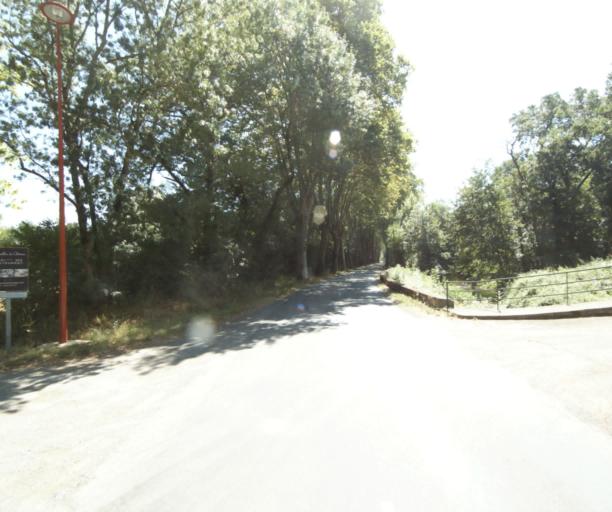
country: FR
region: Midi-Pyrenees
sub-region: Departement de la Haute-Garonne
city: Revel
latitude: 43.4959
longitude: 1.9672
